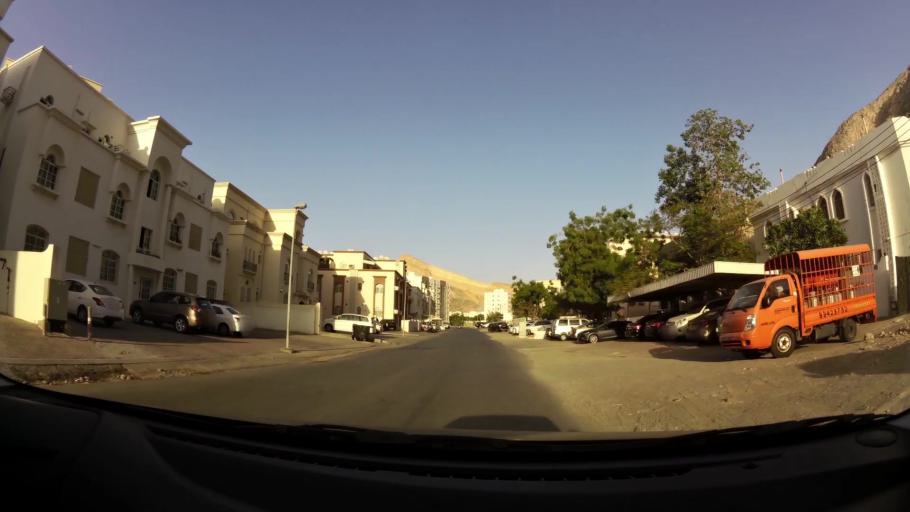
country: OM
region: Muhafazat Masqat
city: Muscat
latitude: 23.5673
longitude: 58.5720
